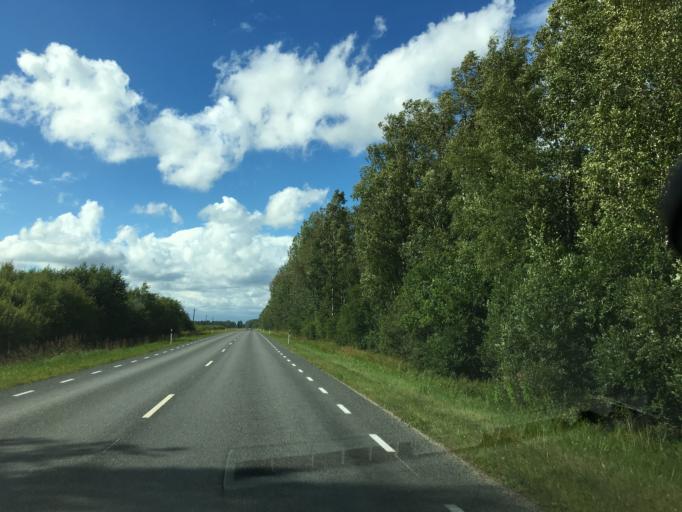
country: EE
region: Paernumaa
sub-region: Vaendra vald (alev)
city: Vandra
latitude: 58.5975
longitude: 25.1454
